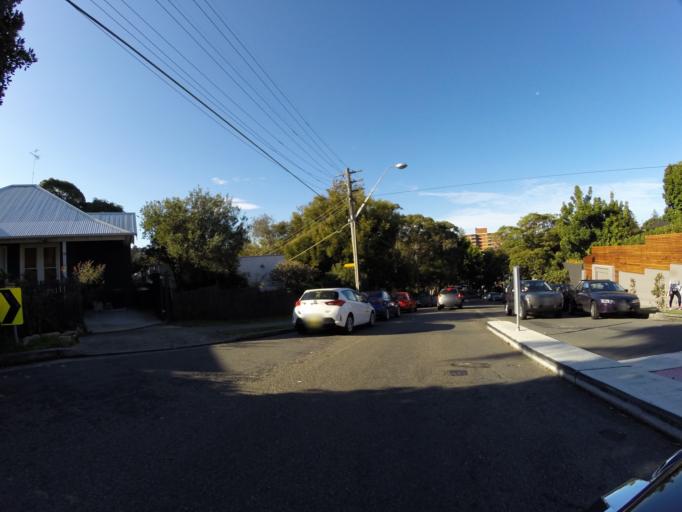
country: AU
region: New South Wales
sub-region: Waverley
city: Bronte
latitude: -33.9020
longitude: 151.2599
